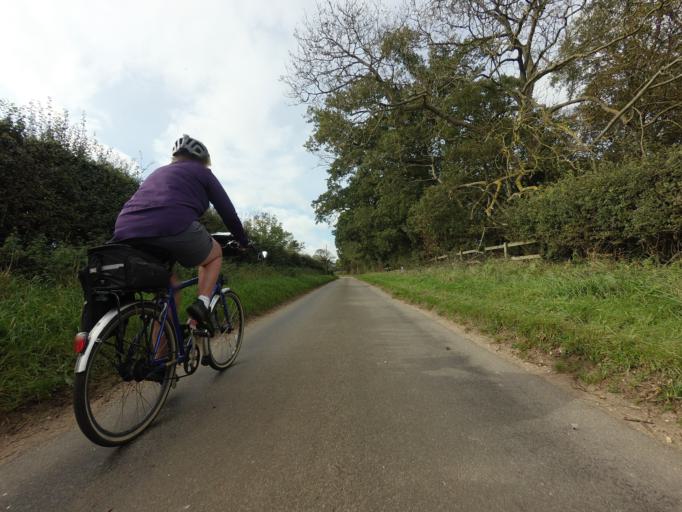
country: GB
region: England
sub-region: Norfolk
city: Wells-next-the-Sea
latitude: 52.9389
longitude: 0.6843
